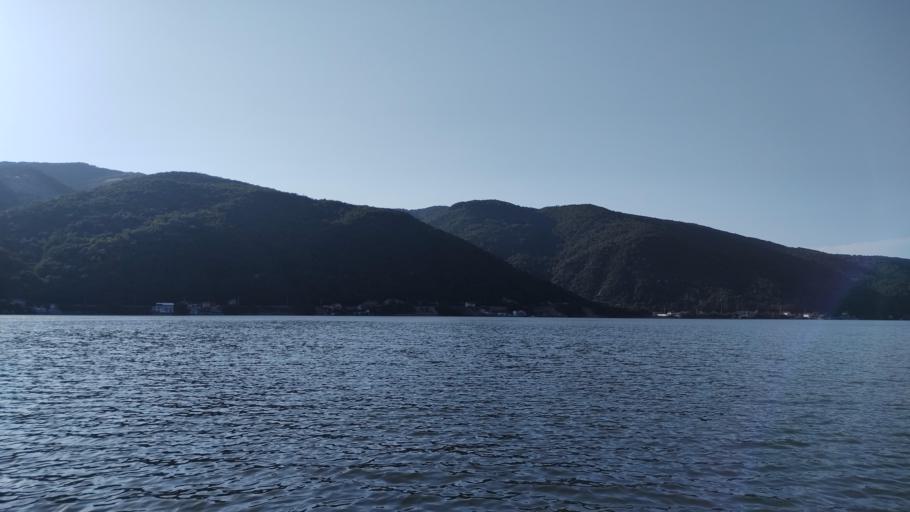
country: RO
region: Mehedinti
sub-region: Comuna Dubova
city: Dubova
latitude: 44.5617
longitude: 22.2341
